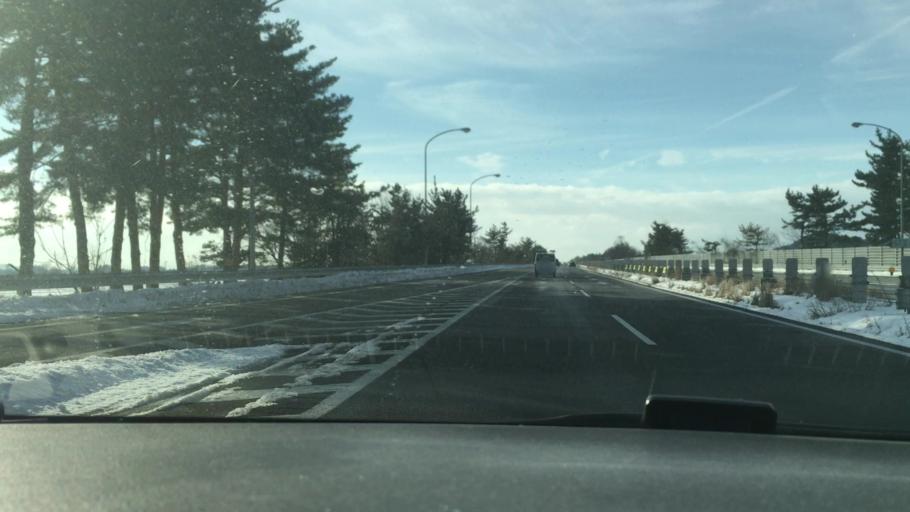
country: JP
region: Iwate
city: Hanamaki
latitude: 39.3684
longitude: 141.0922
